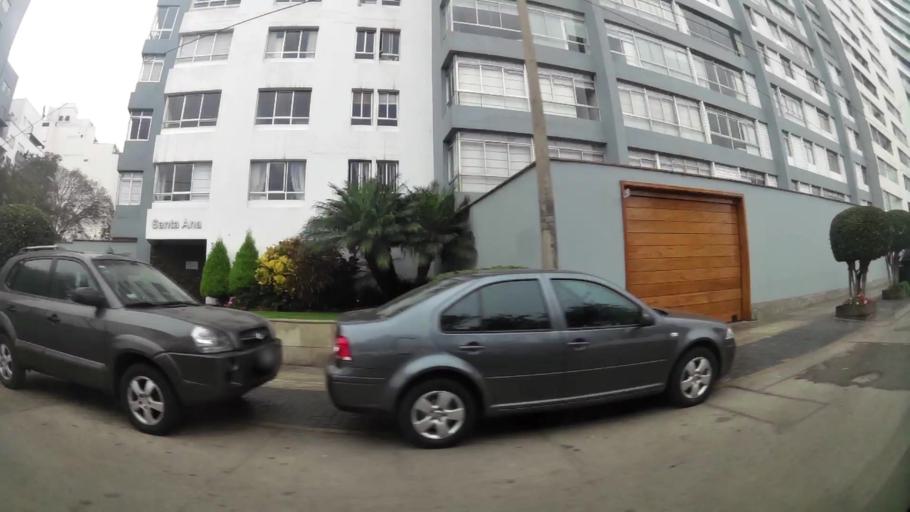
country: PE
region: Lima
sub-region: Lima
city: Surco
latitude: -12.1357
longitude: -77.0260
